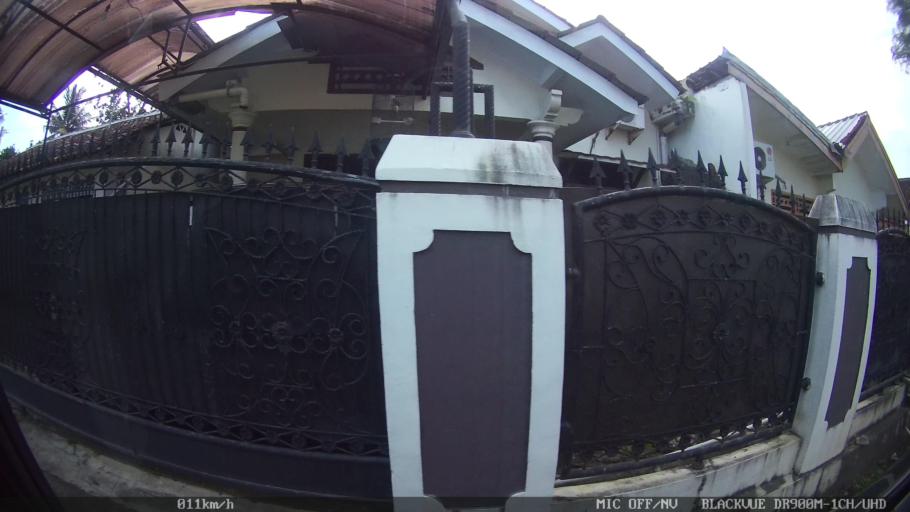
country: ID
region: Lampung
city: Kedaton
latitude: -5.3918
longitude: 105.2083
